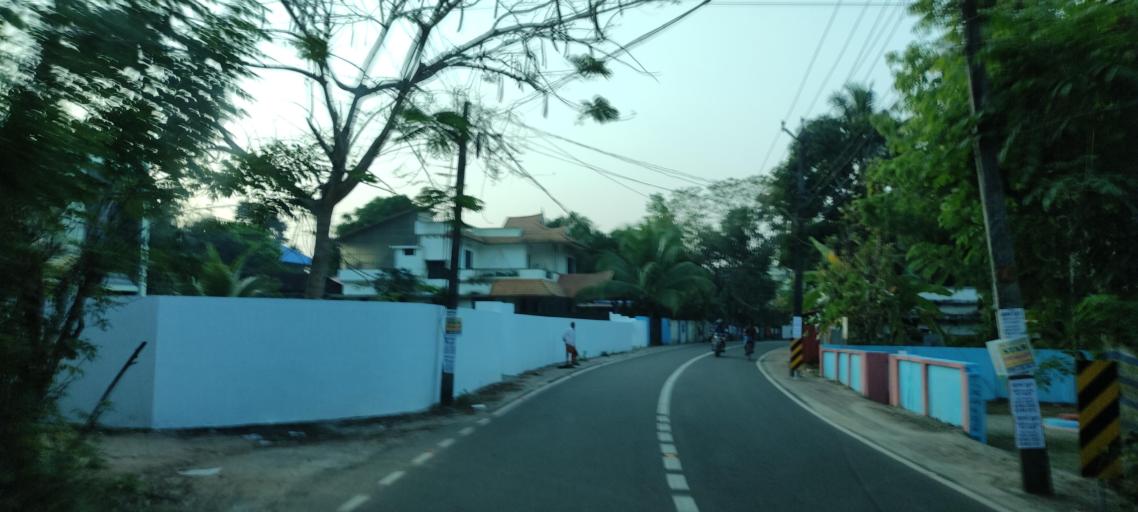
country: IN
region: Kerala
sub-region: Alappuzha
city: Alleppey
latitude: 9.4551
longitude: 76.3450
